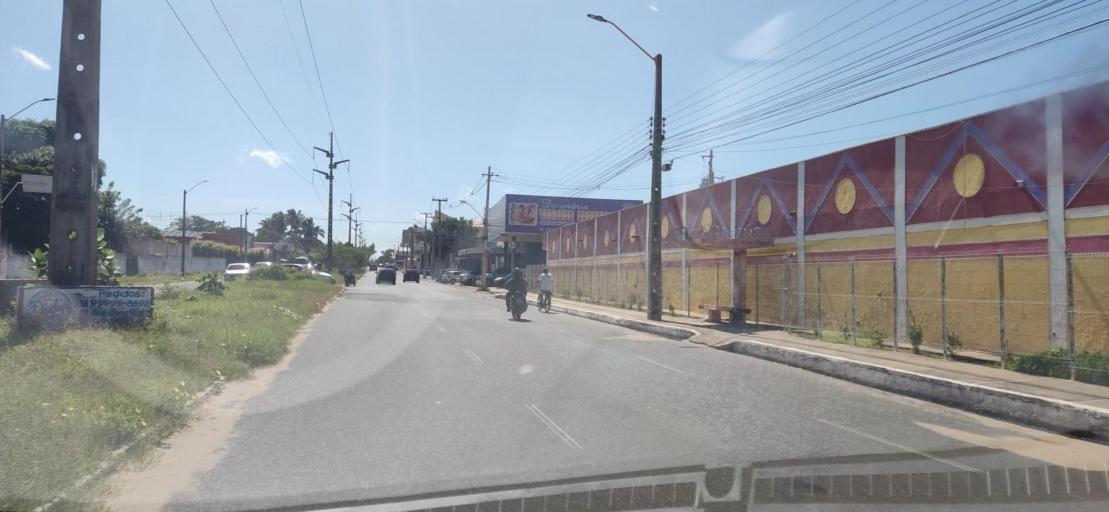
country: BR
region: Piaui
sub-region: Teresina
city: Teresina
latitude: -5.1211
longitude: -42.8060
